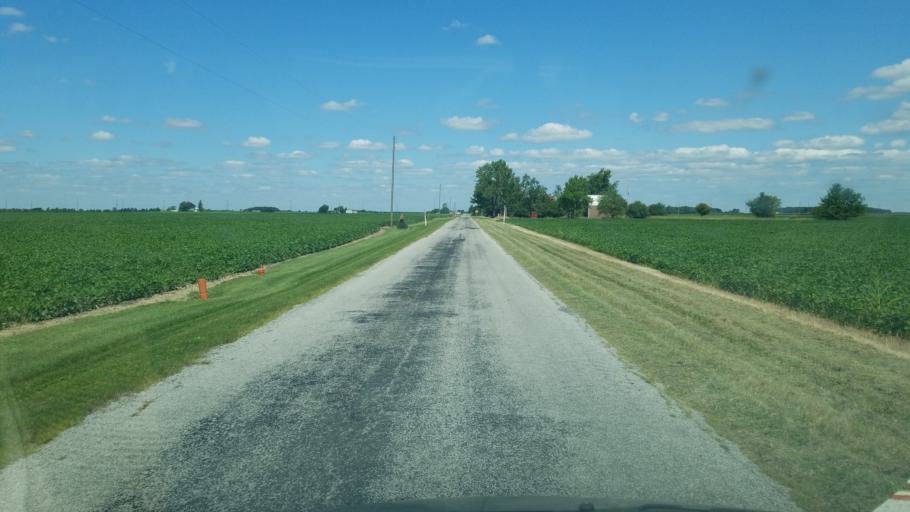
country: US
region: Ohio
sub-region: Fulton County
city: Delta
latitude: 41.6949
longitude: -84.0172
